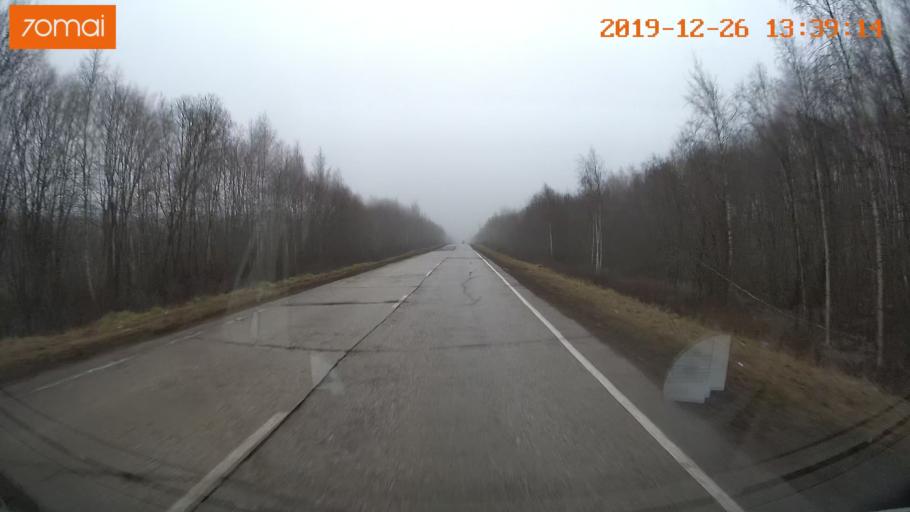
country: RU
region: Vologda
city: Sheksna
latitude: 58.7541
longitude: 38.4072
